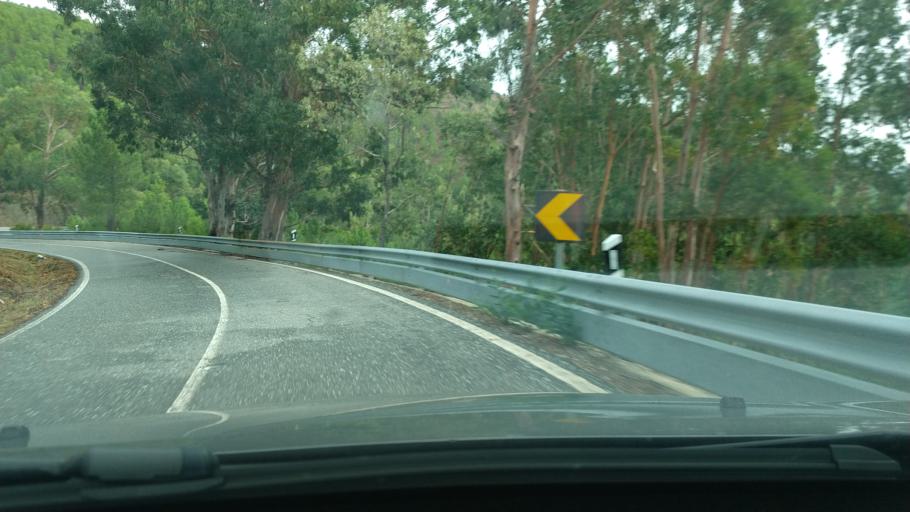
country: PT
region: Castelo Branco
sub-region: Covilha
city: Covilha
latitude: 40.2341
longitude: -7.6671
